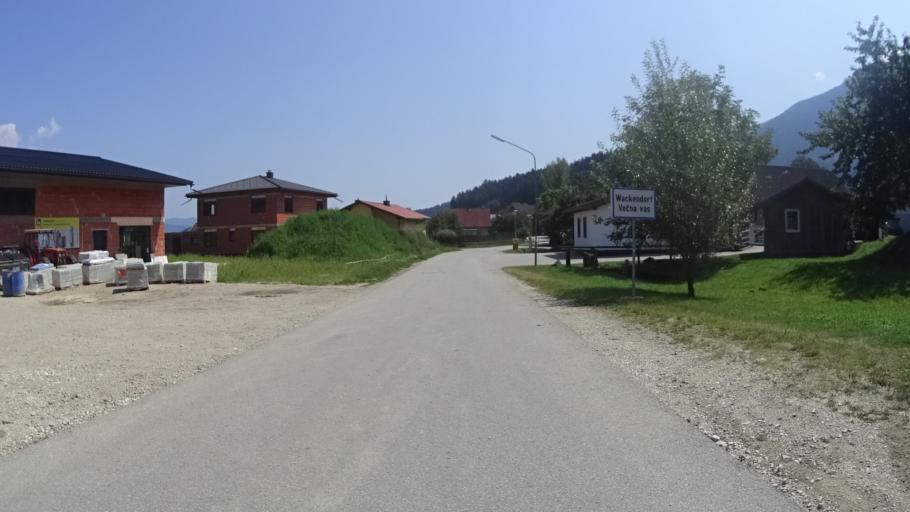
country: AT
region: Carinthia
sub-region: Politischer Bezirk Volkermarkt
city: Globasnitz
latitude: 46.5558
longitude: 14.7198
